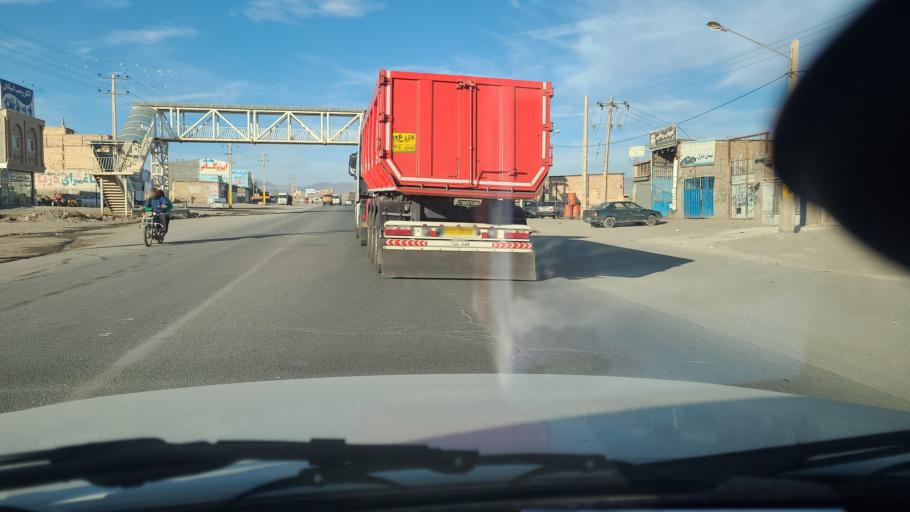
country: IR
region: Razavi Khorasan
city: Sabzevar
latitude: 36.2212
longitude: 57.6515
